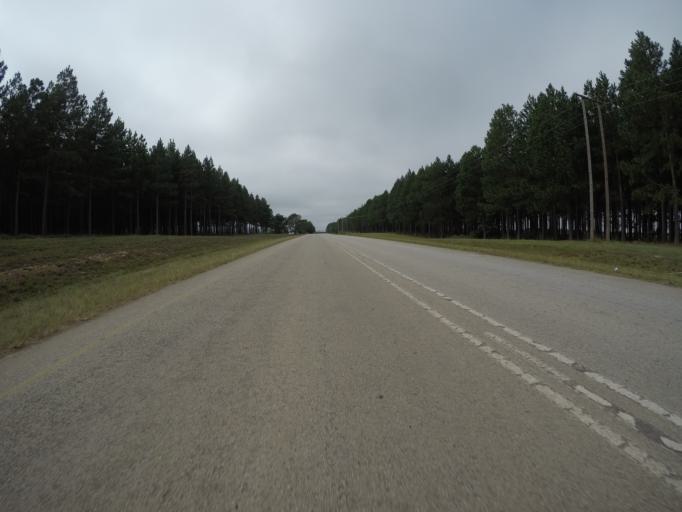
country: ZA
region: Eastern Cape
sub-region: Cacadu District Municipality
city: Kareedouw
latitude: -33.9956
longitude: 24.1299
